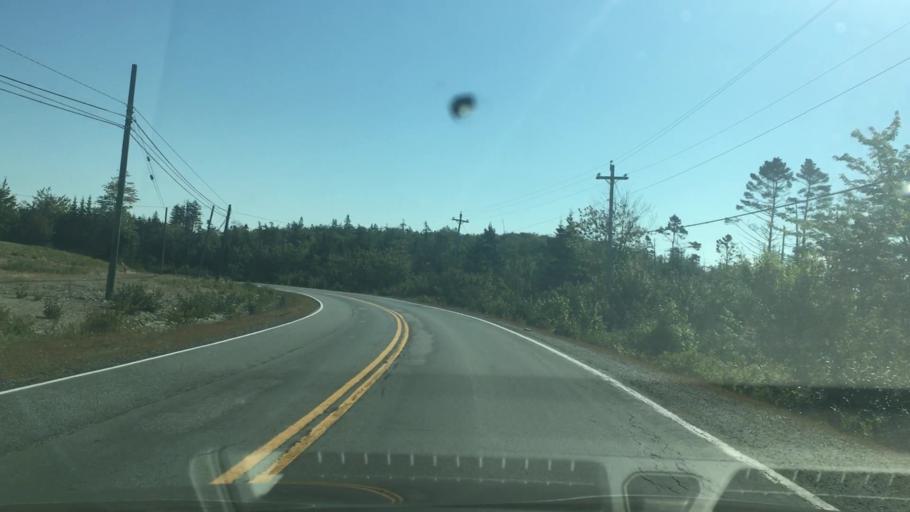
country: CA
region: Nova Scotia
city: Cole Harbour
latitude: 44.7750
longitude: -63.0532
